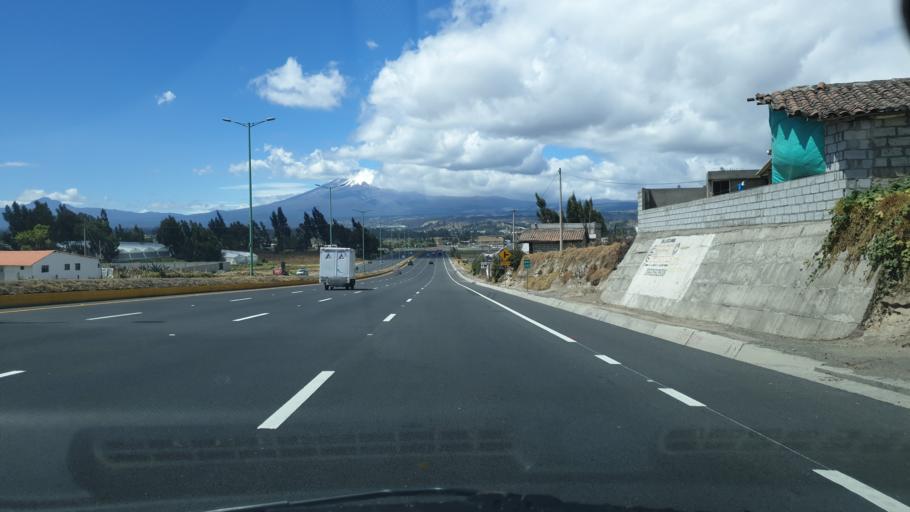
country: EC
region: Cotopaxi
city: Saquisili
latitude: -0.8764
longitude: -78.6444
